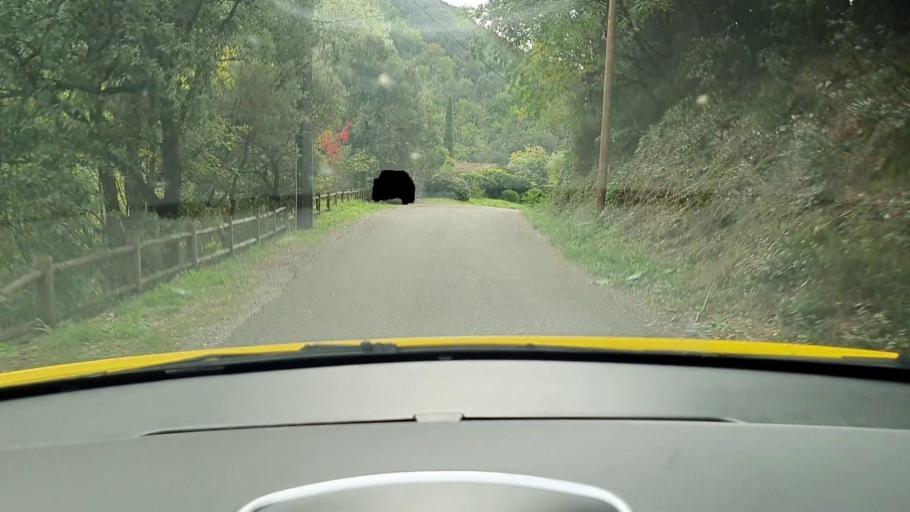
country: FR
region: Languedoc-Roussillon
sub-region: Departement du Gard
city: Sumene
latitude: 44.0104
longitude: 3.6601
